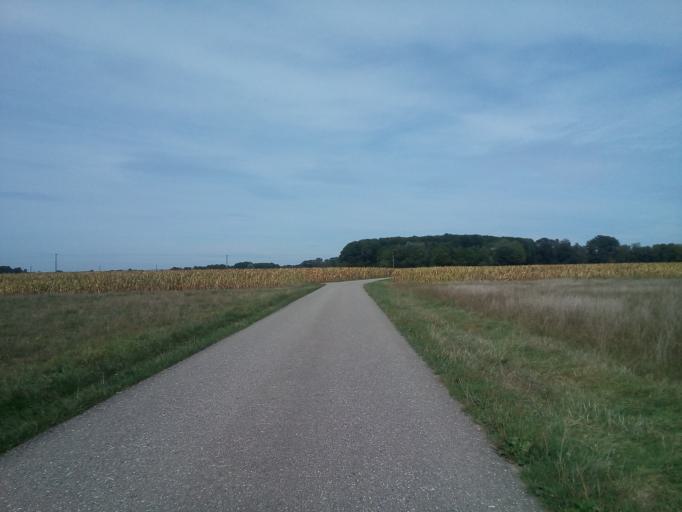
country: DE
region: Baden-Wuerttemberg
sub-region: Karlsruhe Region
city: Zell
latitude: 48.7031
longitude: 8.0455
